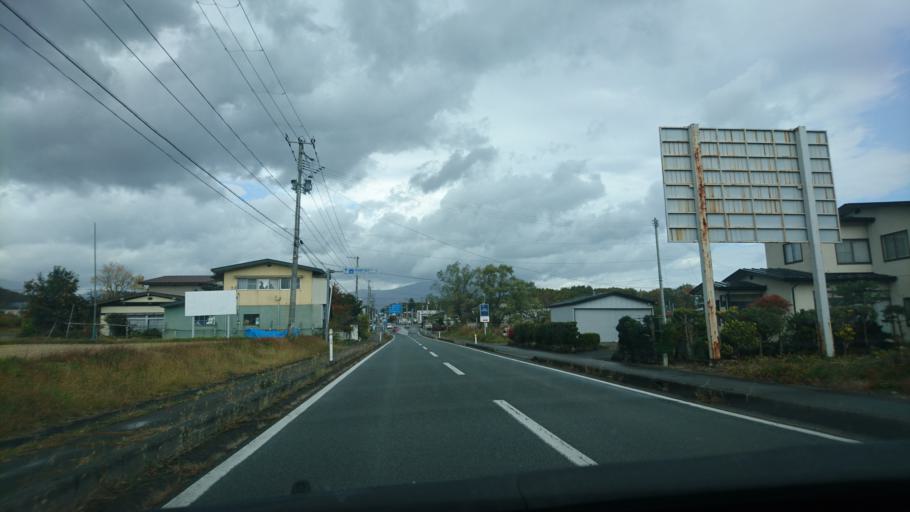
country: JP
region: Iwate
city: Shizukuishi
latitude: 39.6957
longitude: 141.0235
